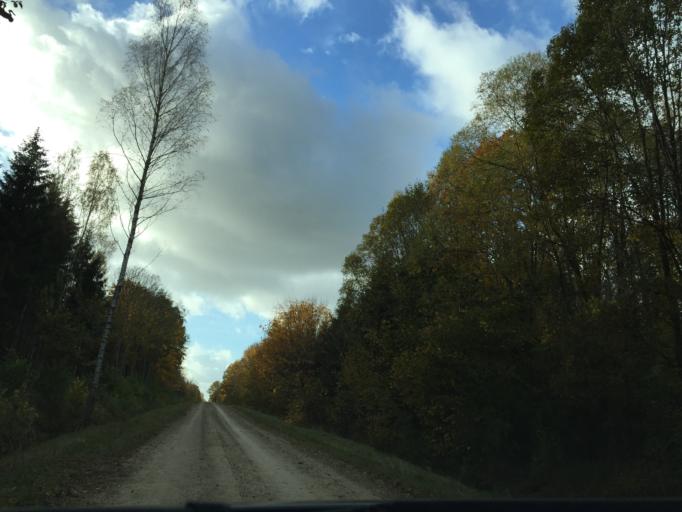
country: LV
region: Ogre
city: Jumprava
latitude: 56.7398
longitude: 24.9433
